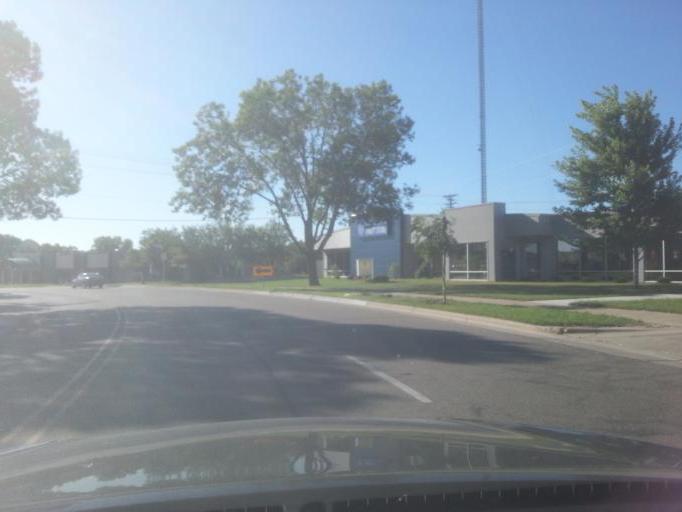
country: US
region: Wisconsin
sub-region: Dane County
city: Middleton
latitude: 43.0539
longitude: -89.4889
